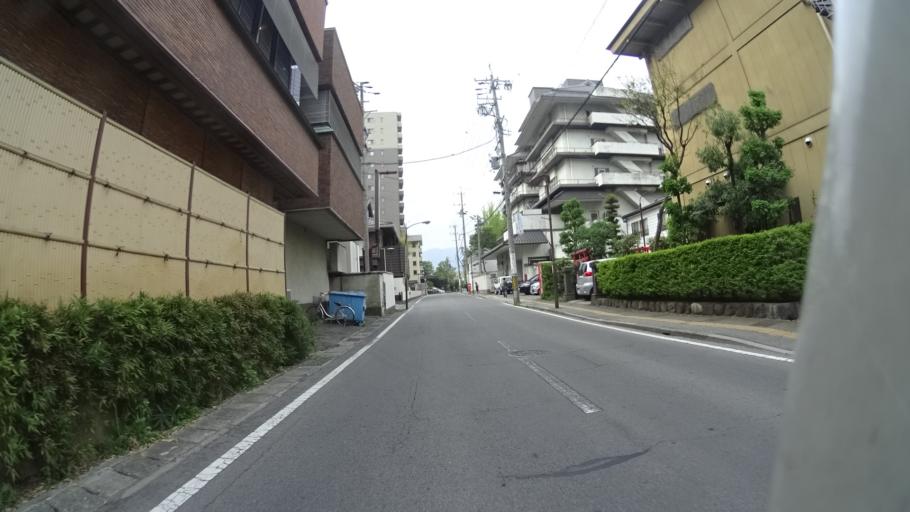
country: JP
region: Nagano
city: Suwa
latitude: 36.0494
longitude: 138.1142
